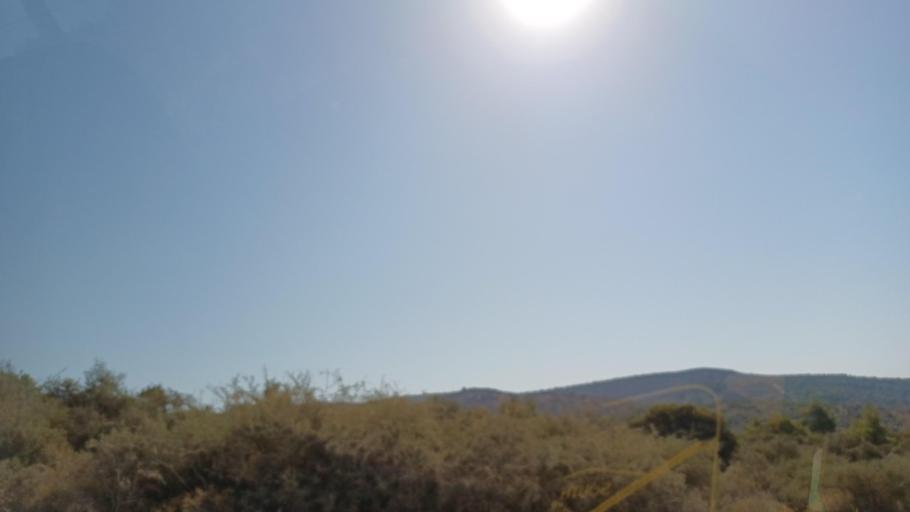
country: CY
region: Limassol
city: Pissouri
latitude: 34.7231
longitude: 32.6786
